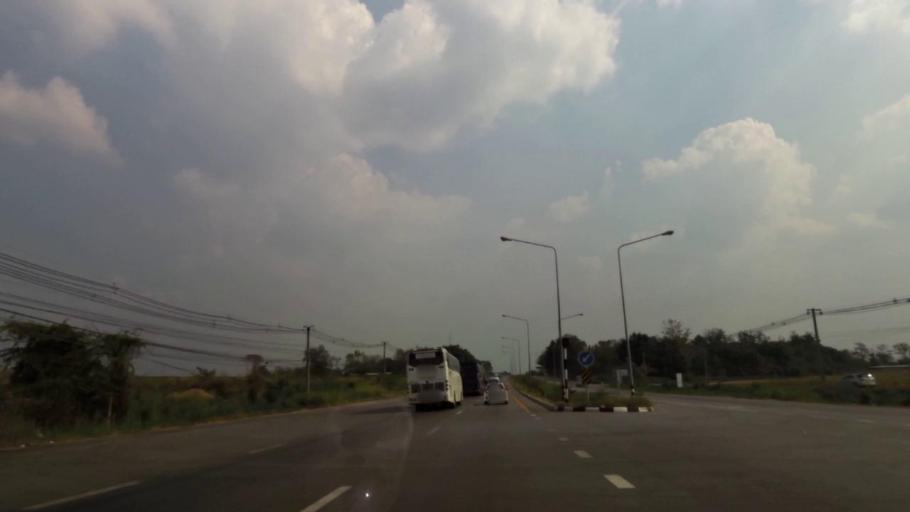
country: TH
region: Chon Buri
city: Nong Yai
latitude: 13.1402
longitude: 101.3430
